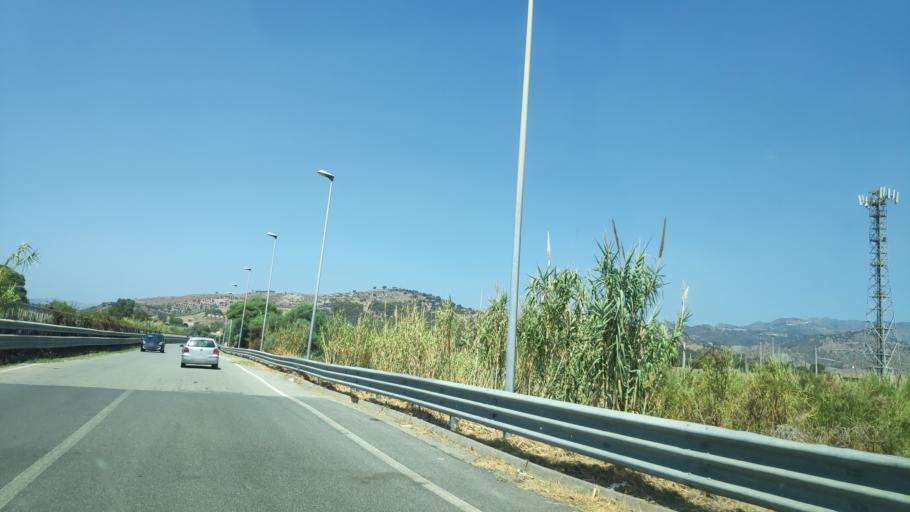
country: IT
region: Calabria
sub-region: Provincia di Reggio Calabria
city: Palizzi Marina
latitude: 37.9214
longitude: 15.9575
